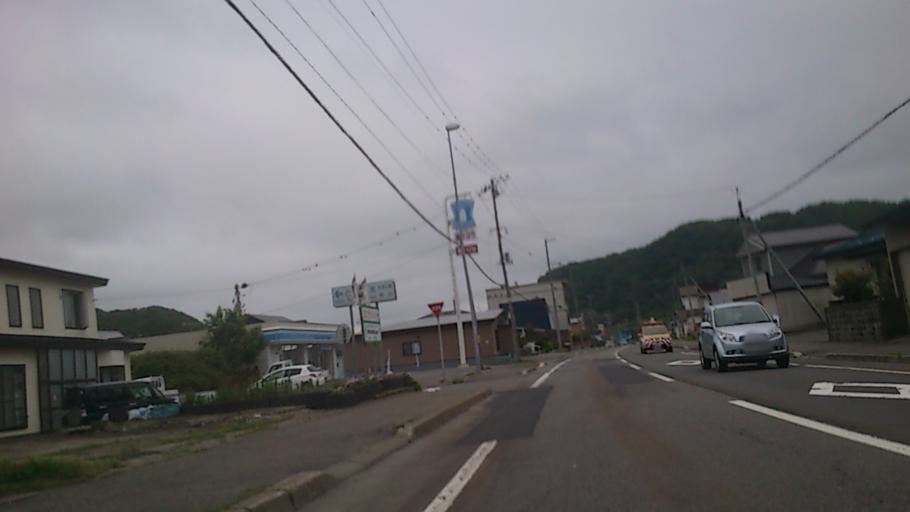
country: JP
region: Hokkaido
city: Kamiiso
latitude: 41.9765
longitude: 140.1355
